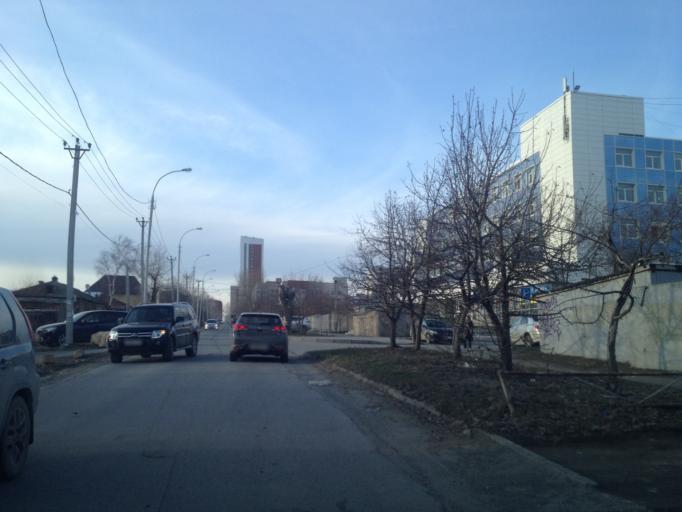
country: RU
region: Sverdlovsk
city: Yekaterinburg
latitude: 56.8015
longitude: 60.5978
